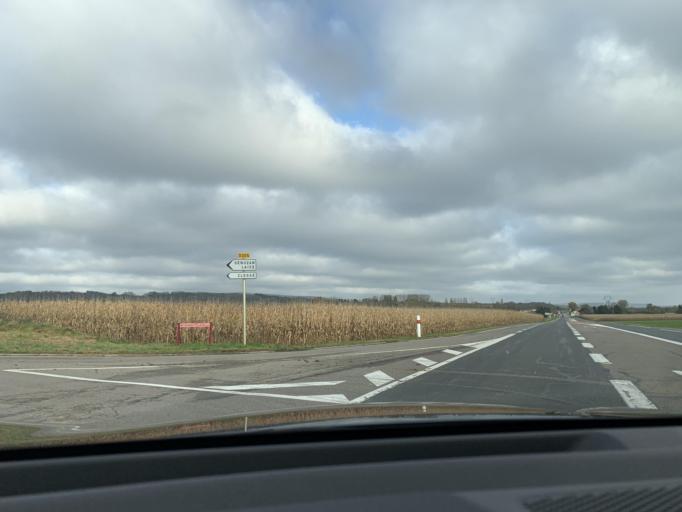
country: FR
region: Bourgogne
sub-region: Departement de Saone-et-Loire
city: Saint-Martin-Belle-Roche
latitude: 46.3977
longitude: 4.8749
